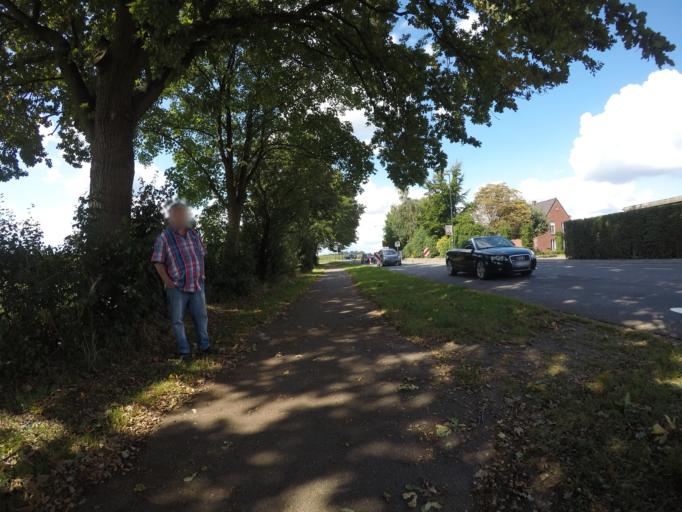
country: DE
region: North Rhine-Westphalia
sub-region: Regierungsbezirk Dusseldorf
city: Hamminkeln
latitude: 51.7329
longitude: 6.5816
